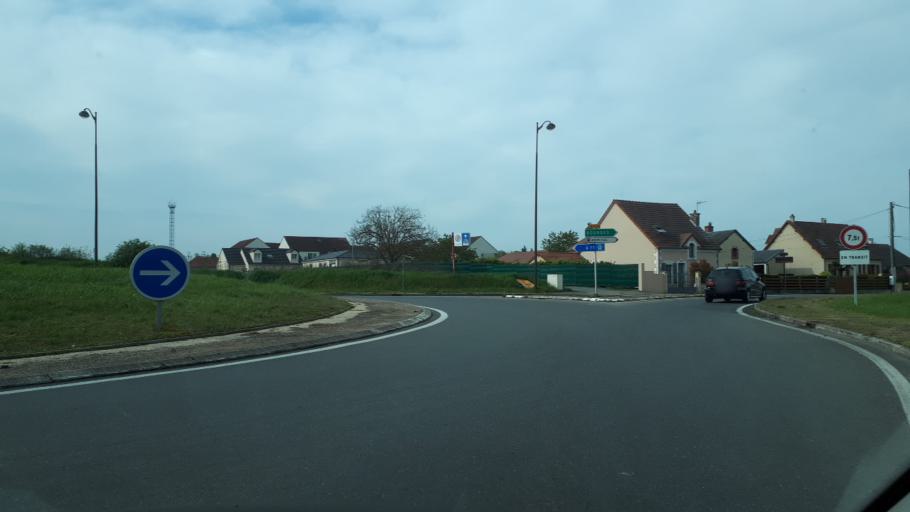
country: FR
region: Centre
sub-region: Departement du Cher
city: Bourges
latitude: 47.0841
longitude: 2.4421
